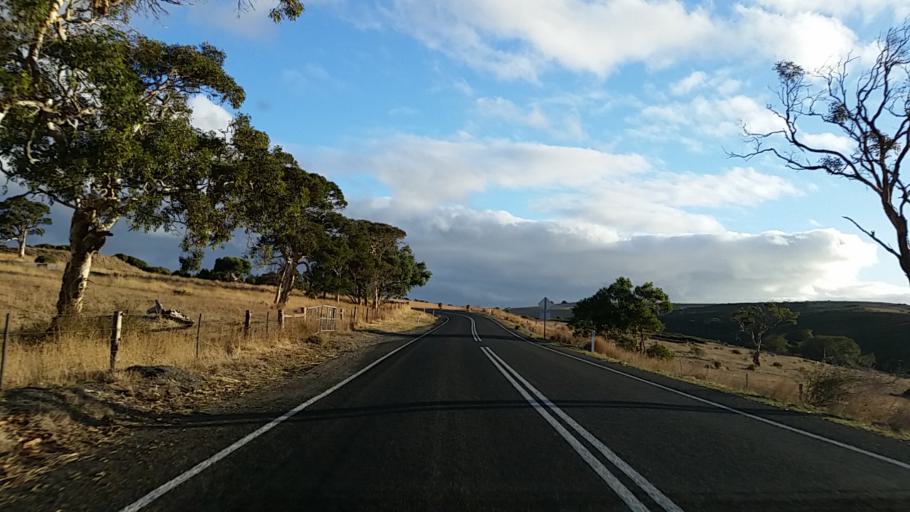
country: AU
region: South Australia
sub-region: Yankalilla
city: Normanville
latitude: -35.5556
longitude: 138.1991
